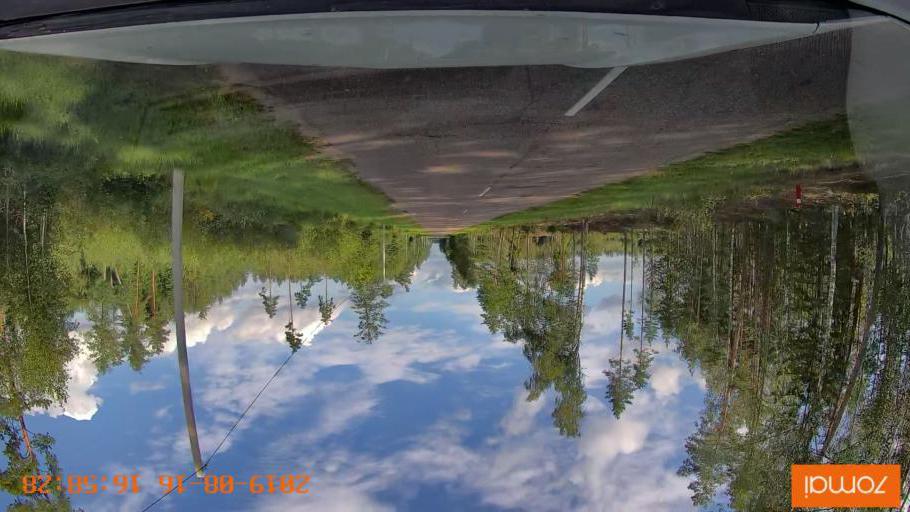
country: BY
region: Mogilev
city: Hlusha
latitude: 53.2697
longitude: 28.8336
